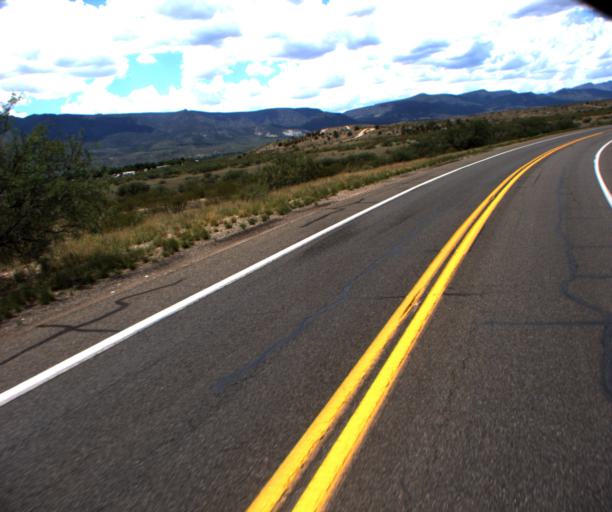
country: US
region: Arizona
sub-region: Yavapai County
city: Camp Verde
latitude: 34.5272
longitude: -111.8044
